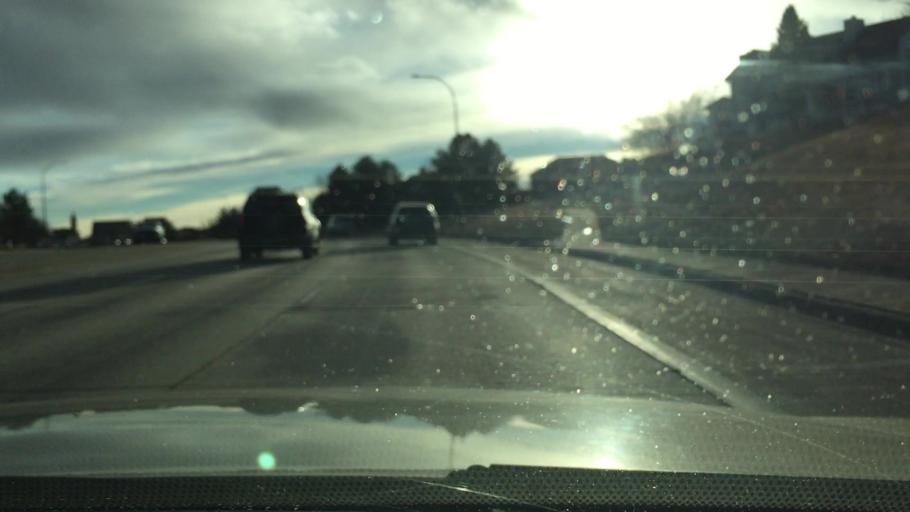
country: US
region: Colorado
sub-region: Douglas County
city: Highlands Ranch
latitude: 39.5396
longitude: -104.9587
